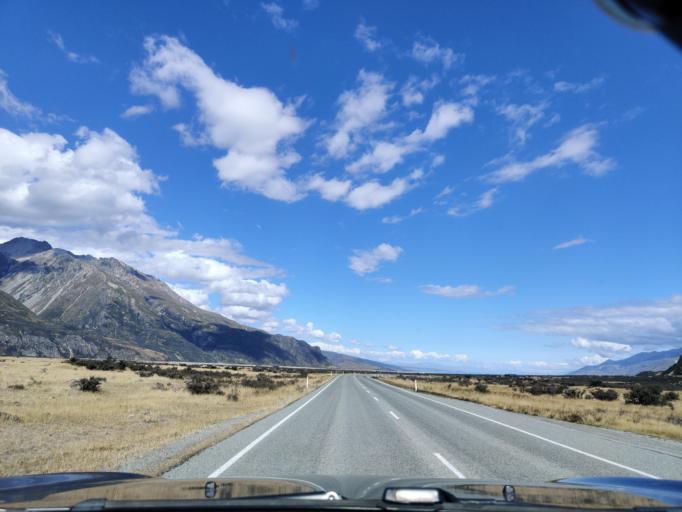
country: NZ
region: Canterbury
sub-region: Timaru District
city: Pleasant Point
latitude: -43.7491
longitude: 170.1165
